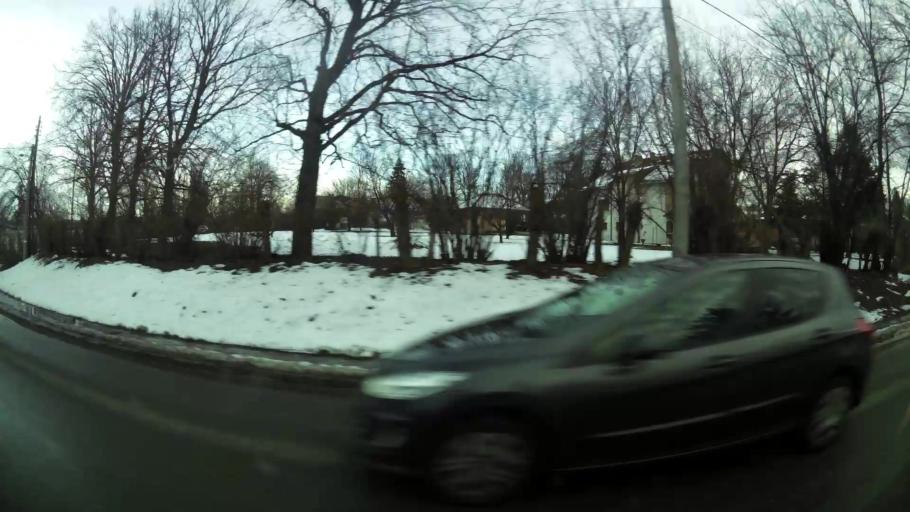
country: RS
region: Central Serbia
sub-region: Belgrade
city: Vozdovac
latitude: 44.7498
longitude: 20.4768
